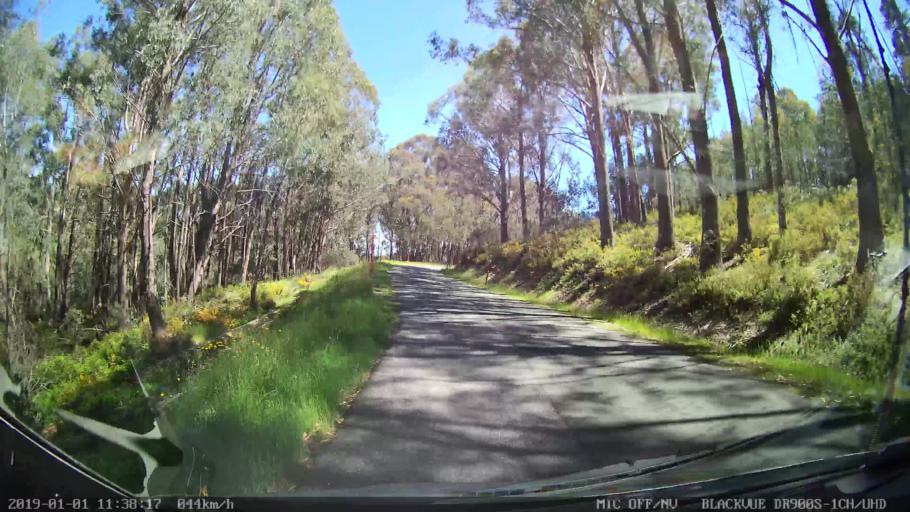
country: AU
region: New South Wales
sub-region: Snowy River
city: Jindabyne
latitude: -35.9352
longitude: 148.3870
